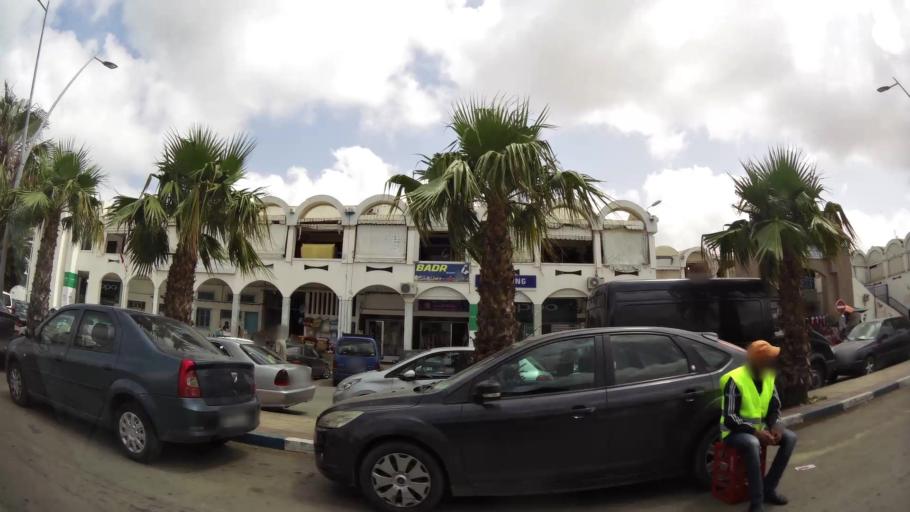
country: MA
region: Oriental
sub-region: Nador
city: Nador
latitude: 35.1782
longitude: -2.9233
